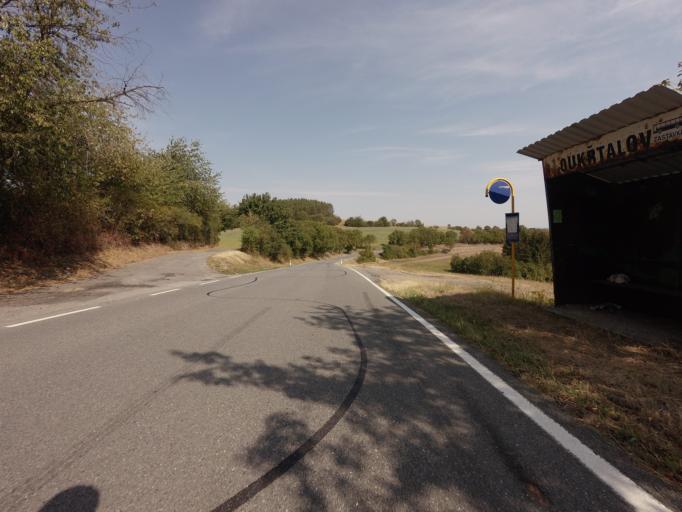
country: CZ
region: Central Bohemia
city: Petrovice
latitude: 49.5845
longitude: 14.3791
